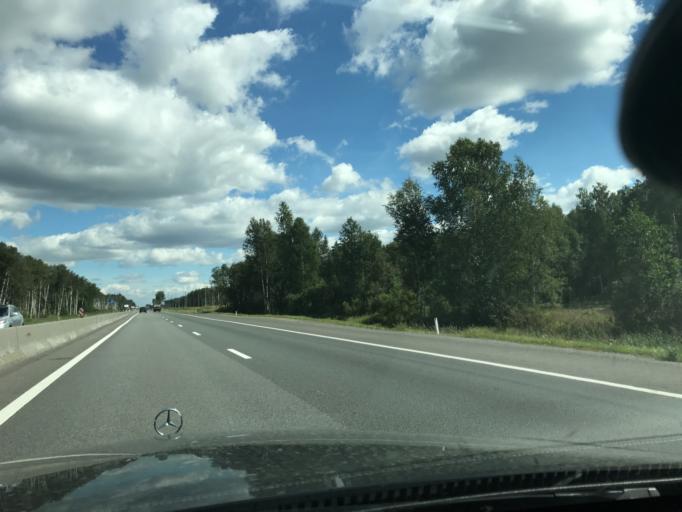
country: RU
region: Nizjnij Novgorod
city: Pyra
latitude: 56.2906
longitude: 43.2907
